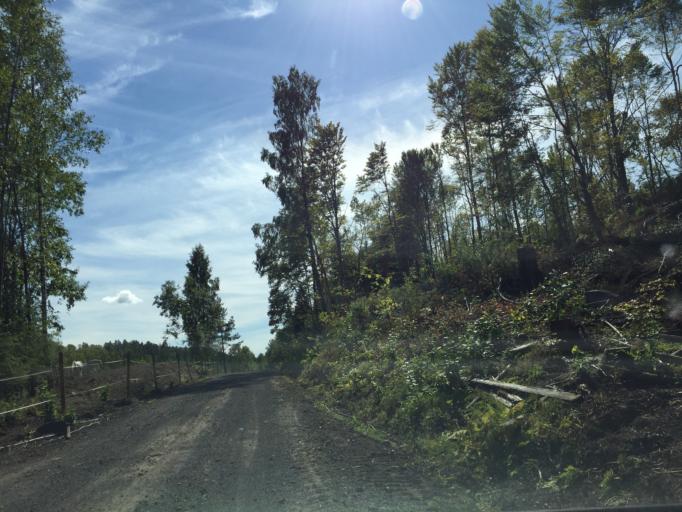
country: NO
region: Vestfold
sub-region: Hof
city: Hof
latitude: 59.4551
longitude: 10.1486
